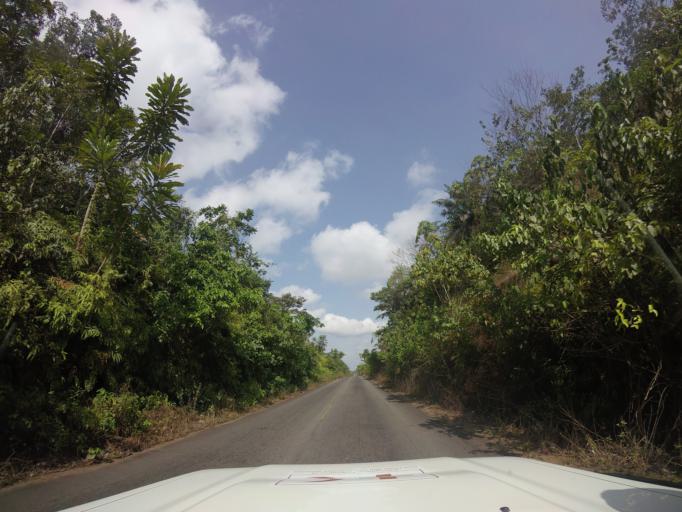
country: LR
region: Bomi
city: Tubmanburg
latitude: 6.6939
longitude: -10.8967
